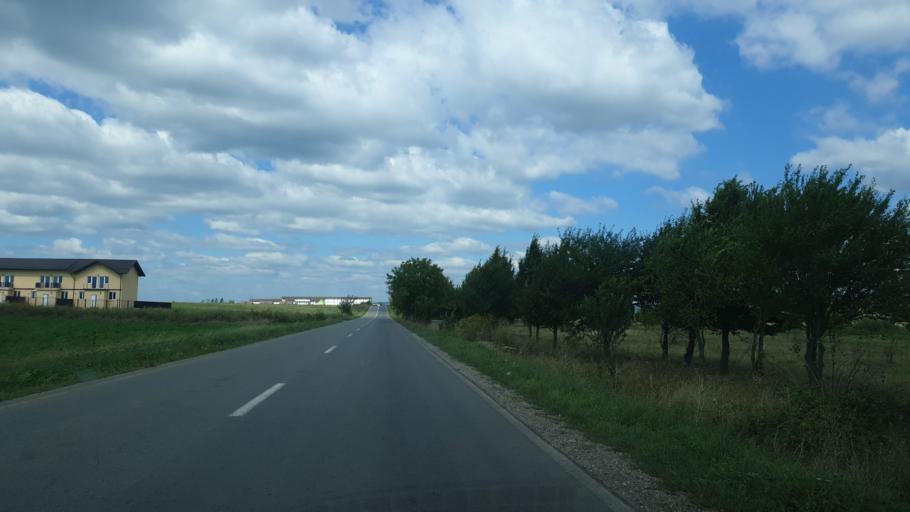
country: RO
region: Brasov
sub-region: Comuna Sanpetru
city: Sanpetru
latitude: 45.7215
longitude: 25.6277
